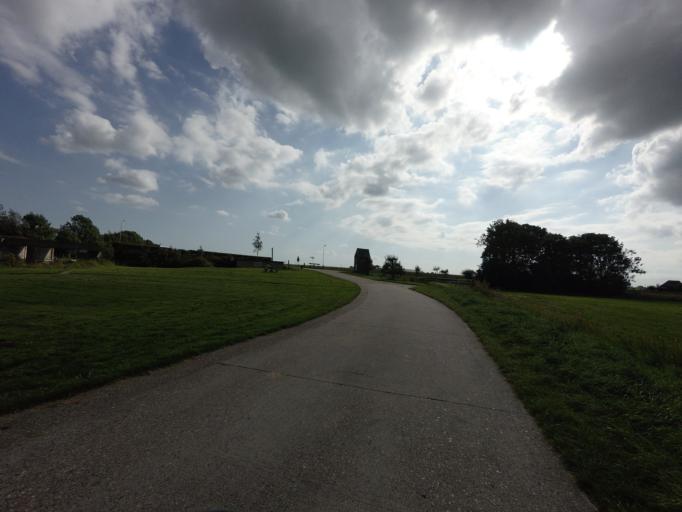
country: NL
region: Friesland
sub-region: Sudwest Fryslan
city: Scharnegoutum
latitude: 53.0769
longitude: 5.6308
